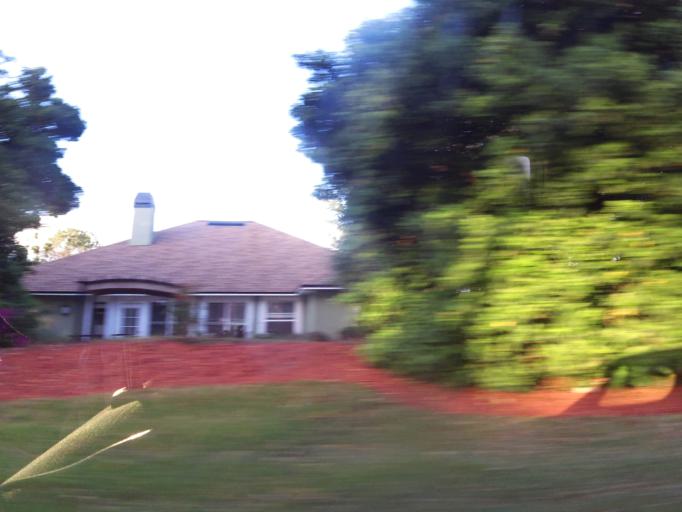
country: US
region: Florida
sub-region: Duval County
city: Jacksonville Beach
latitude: 30.2652
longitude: -81.4615
